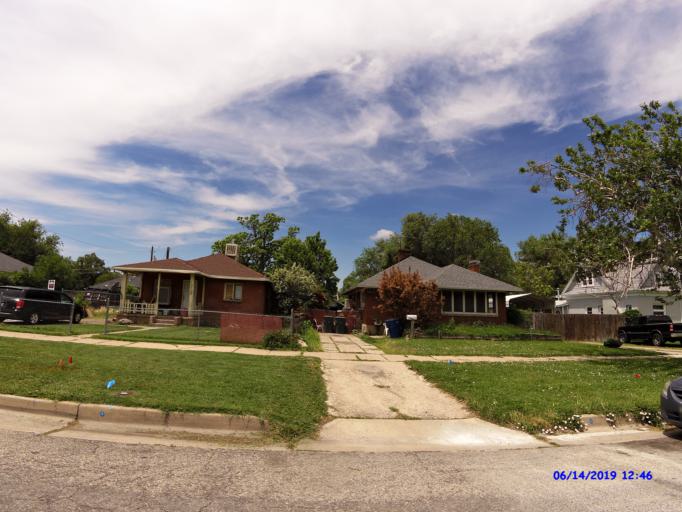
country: US
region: Utah
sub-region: Weber County
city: Ogden
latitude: 41.2279
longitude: -111.9564
